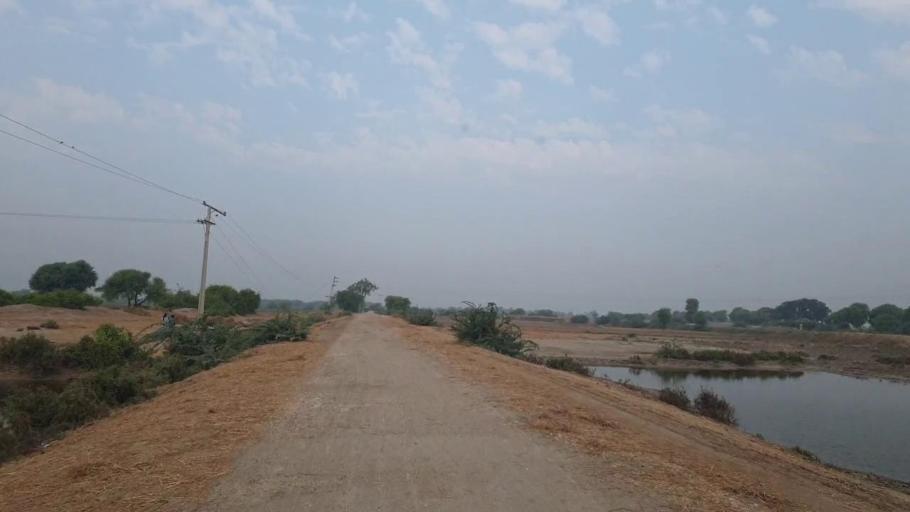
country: PK
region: Sindh
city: Talhar
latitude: 24.8408
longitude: 68.8759
